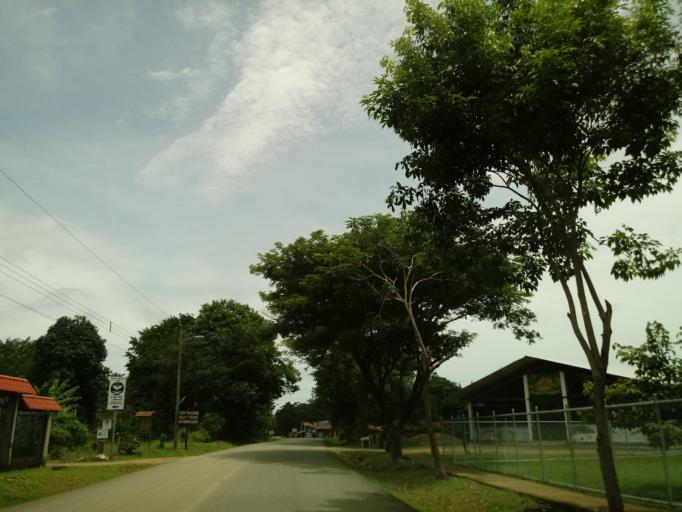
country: CR
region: San Jose
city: Mercedes
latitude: 9.1577
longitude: -83.7428
